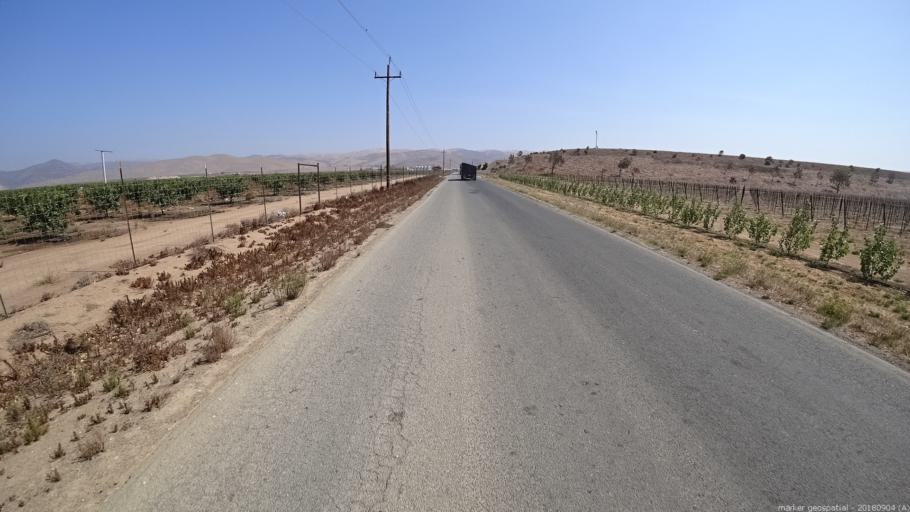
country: US
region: California
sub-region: Monterey County
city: Gonzales
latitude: 36.5297
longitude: -121.4132
